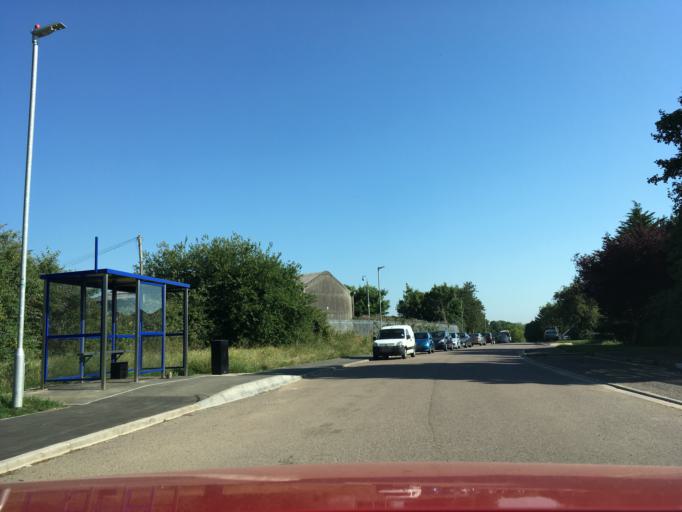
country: GB
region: England
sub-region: South Gloucestershire
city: Pucklechurch
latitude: 51.4815
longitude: -2.4337
